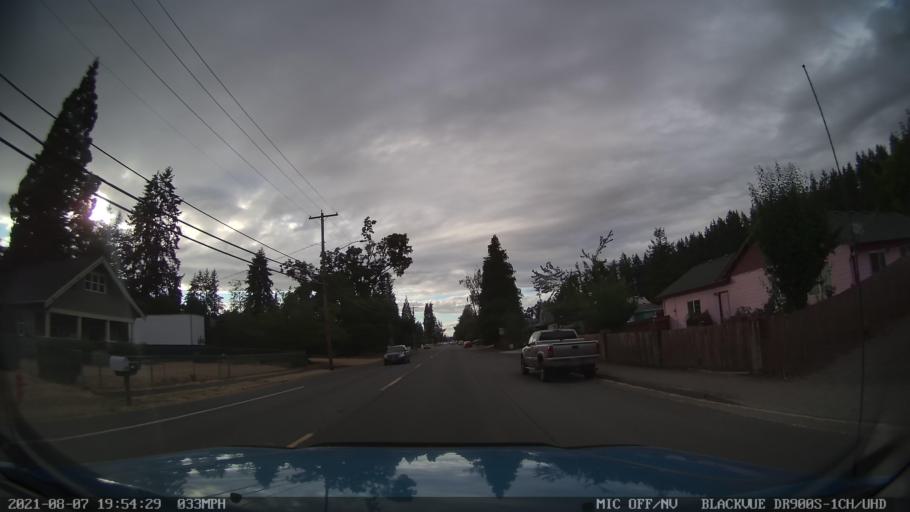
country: US
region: Oregon
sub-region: Marion County
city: Silverton
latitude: 44.9953
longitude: -122.7738
